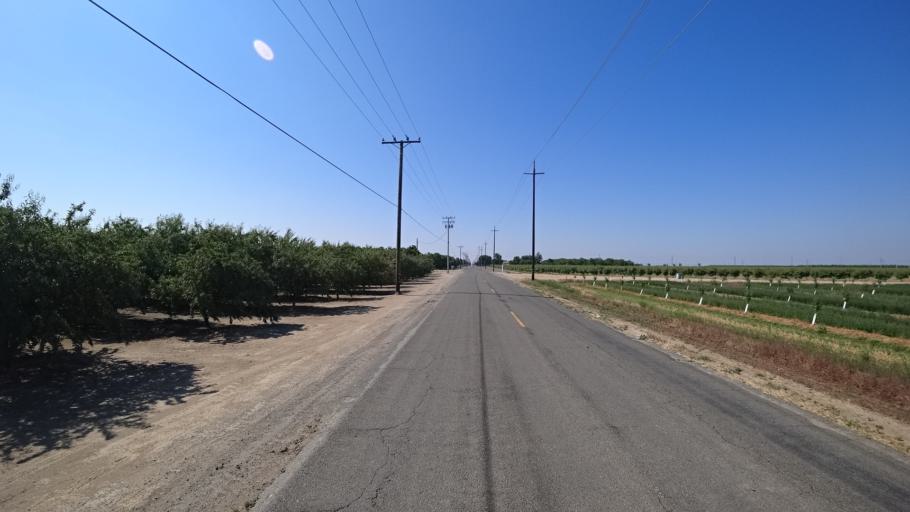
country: US
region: California
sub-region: Kings County
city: Hanford
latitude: 36.3462
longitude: -119.5830
